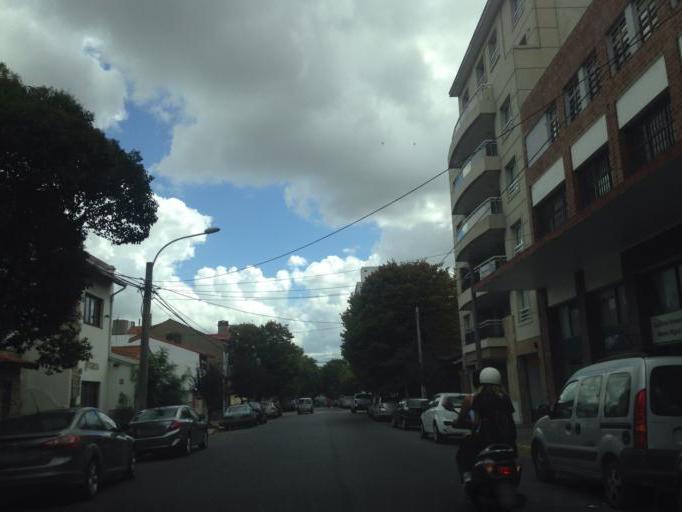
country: AR
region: Buenos Aires
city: Mar del Plata
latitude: -38.0069
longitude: -57.5545
